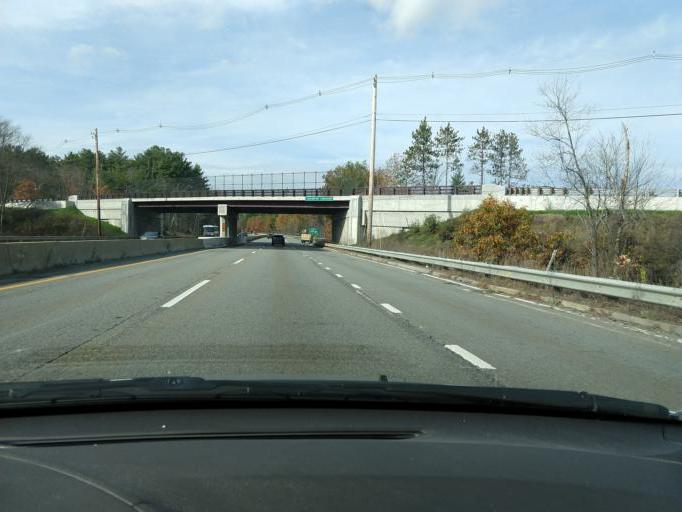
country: US
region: Massachusetts
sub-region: Middlesex County
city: Shirley
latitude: 42.5209
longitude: -71.6349
